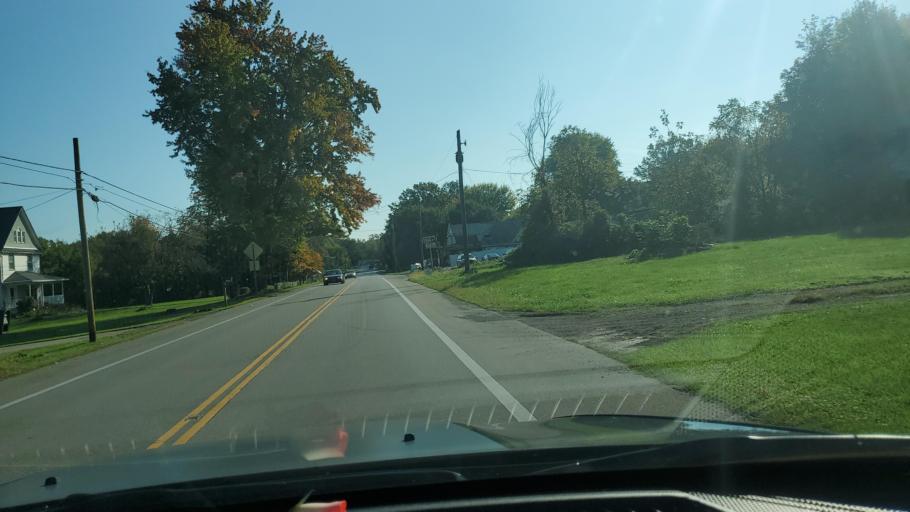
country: US
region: Ohio
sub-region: Trumbull County
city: Hubbard
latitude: 41.1485
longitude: -80.6040
